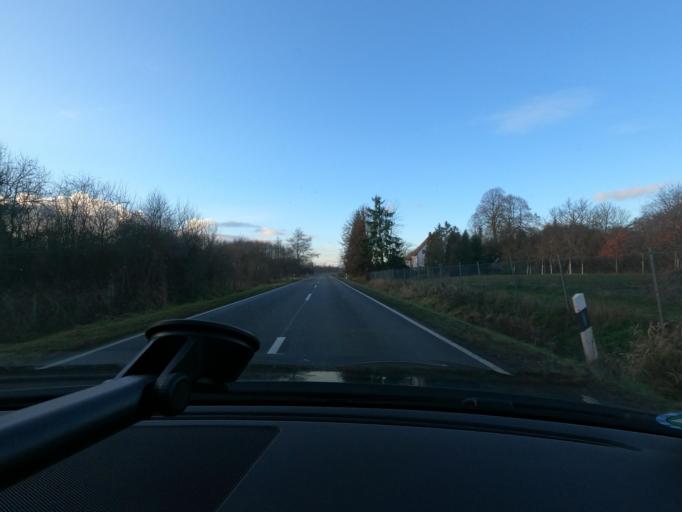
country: DE
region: Lower Saxony
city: Rhumspringe
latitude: 51.5658
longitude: 10.3114
